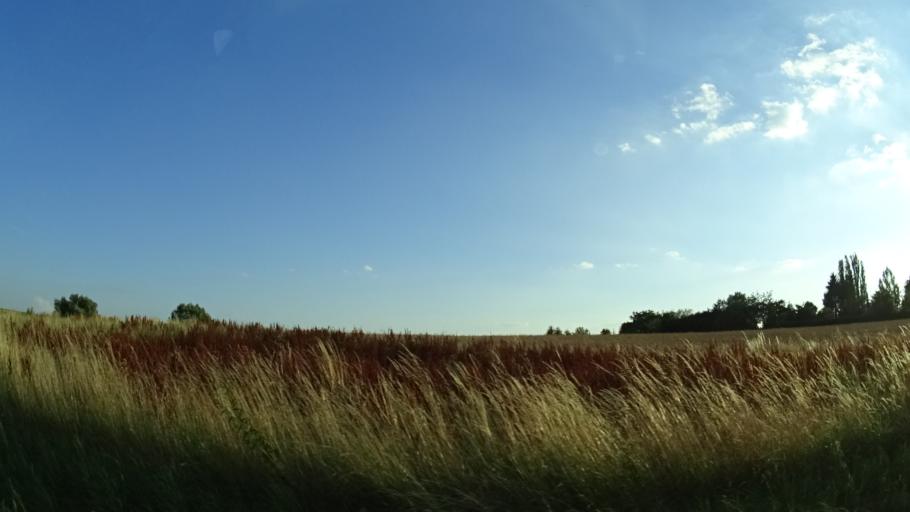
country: DE
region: Thuringia
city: Wolfershausen
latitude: 50.4537
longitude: 10.4431
